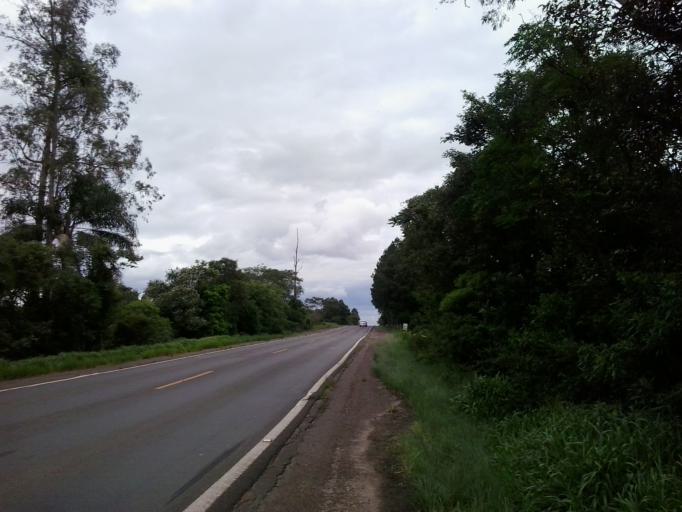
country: BR
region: Rio Grande do Sul
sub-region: Santa Maria
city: Santa Maria
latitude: -29.7319
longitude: -53.5465
